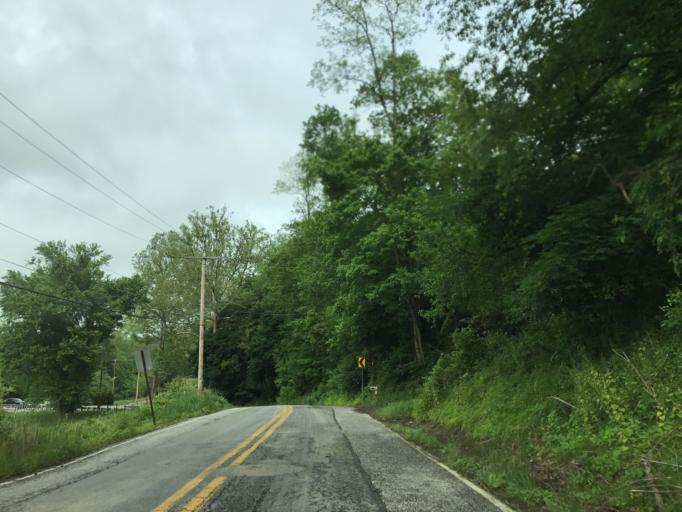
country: US
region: Pennsylvania
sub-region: York County
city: Susquehanna Trails
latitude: 39.7818
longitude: -76.4080
